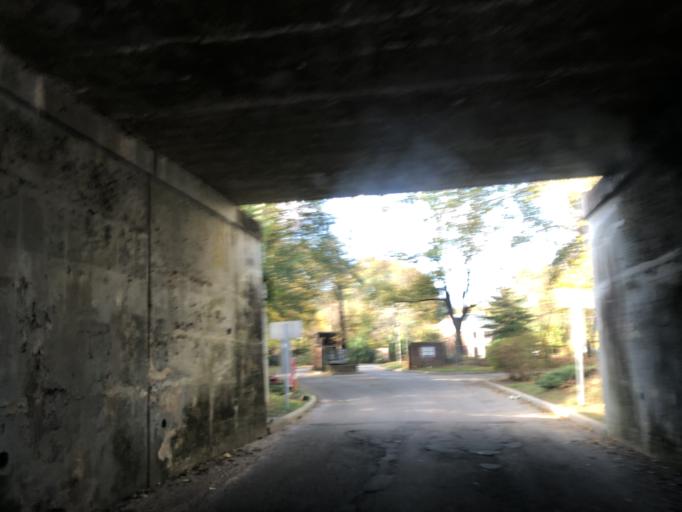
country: US
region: New York
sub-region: Nassau County
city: Greenvale
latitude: 40.8079
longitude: -73.6356
